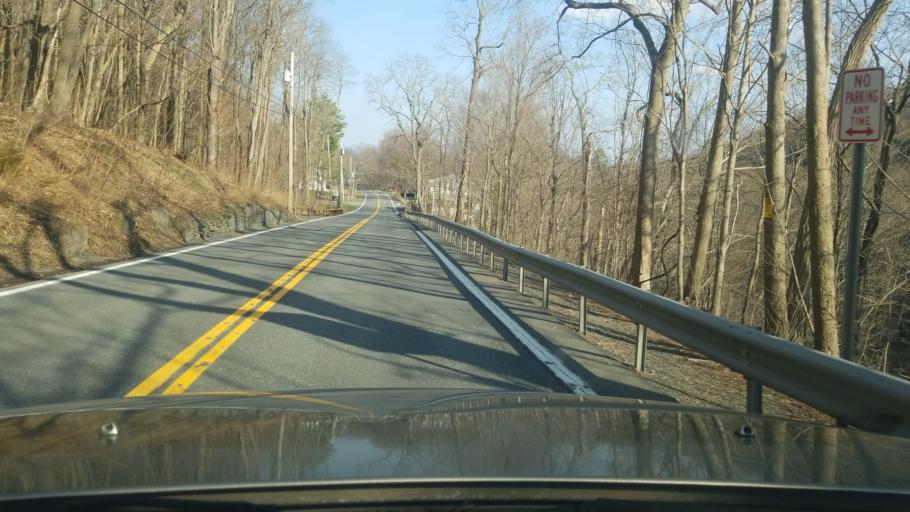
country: US
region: New York
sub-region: Greene County
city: Palenville
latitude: 42.1767
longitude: -74.0323
